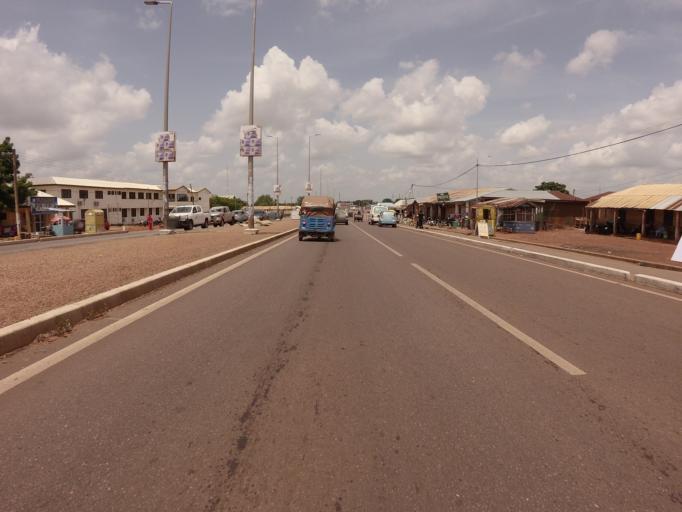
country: GH
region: Northern
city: Tamale
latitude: 9.3995
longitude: -0.8326
